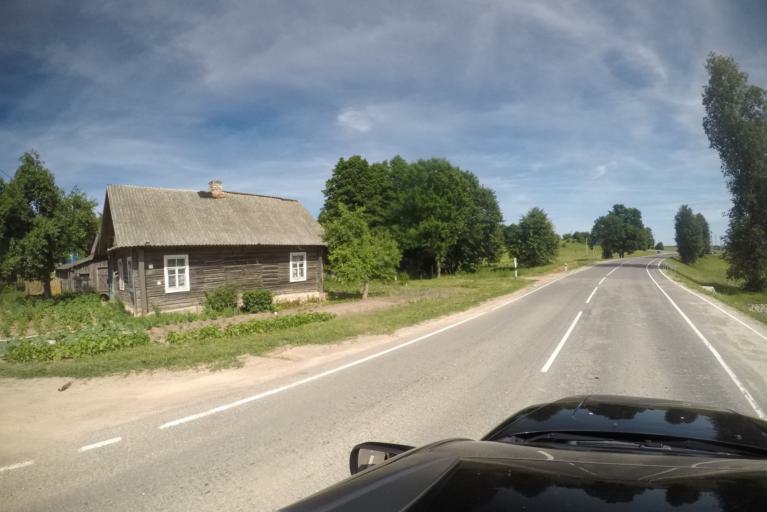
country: BY
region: Grodnenskaya
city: Hal'shany
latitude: 54.2530
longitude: 26.0209
